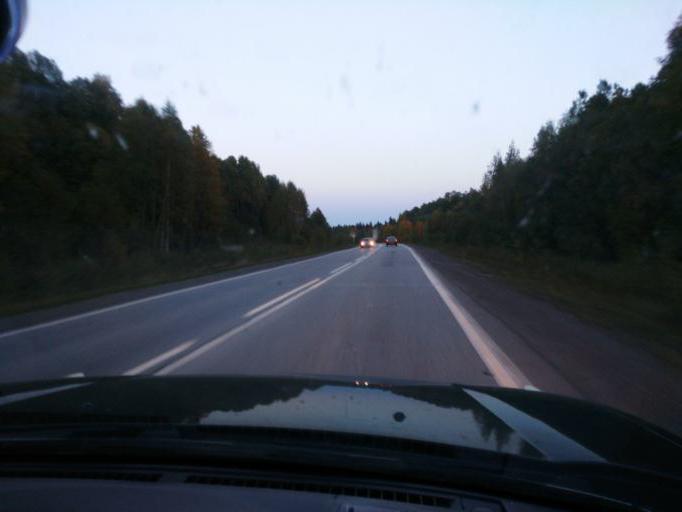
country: RU
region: Perm
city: Verkhnechusovskiye Gorodki
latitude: 58.2656
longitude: 56.9623
